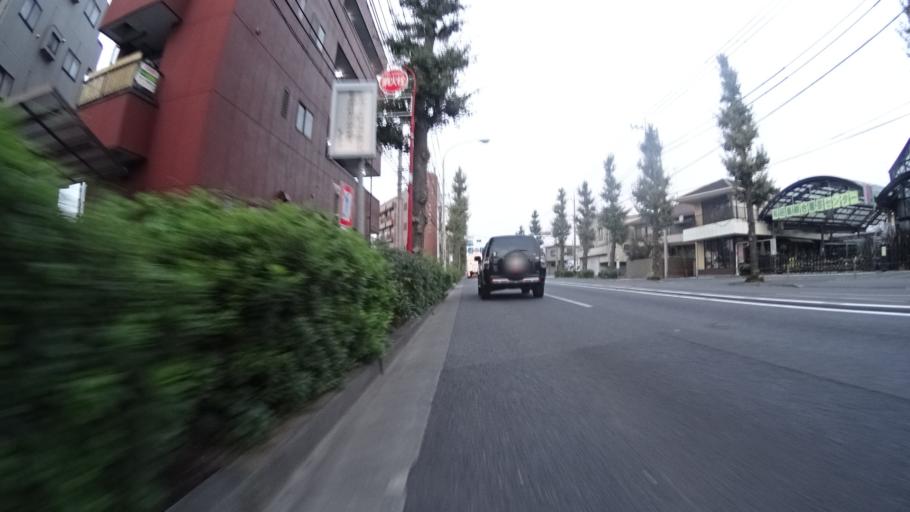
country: JP
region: Tokyo
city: Hino
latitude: 35.6960
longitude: 139.3791
